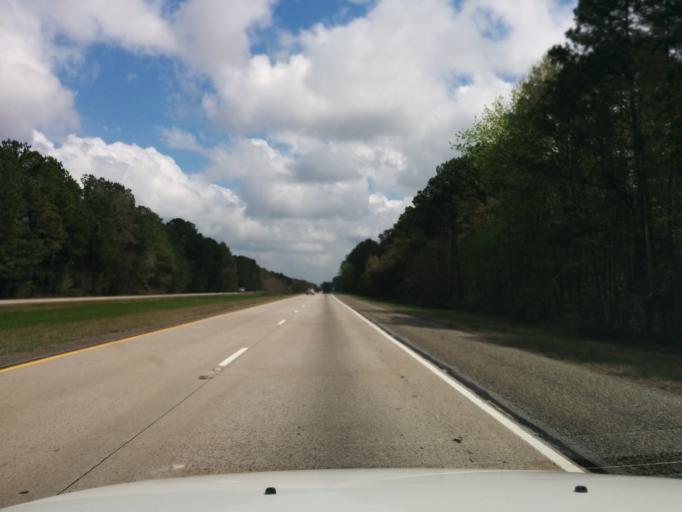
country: US
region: Georgia
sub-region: Bryan County
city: Pembroke
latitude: 32.2308
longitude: -81.6412
